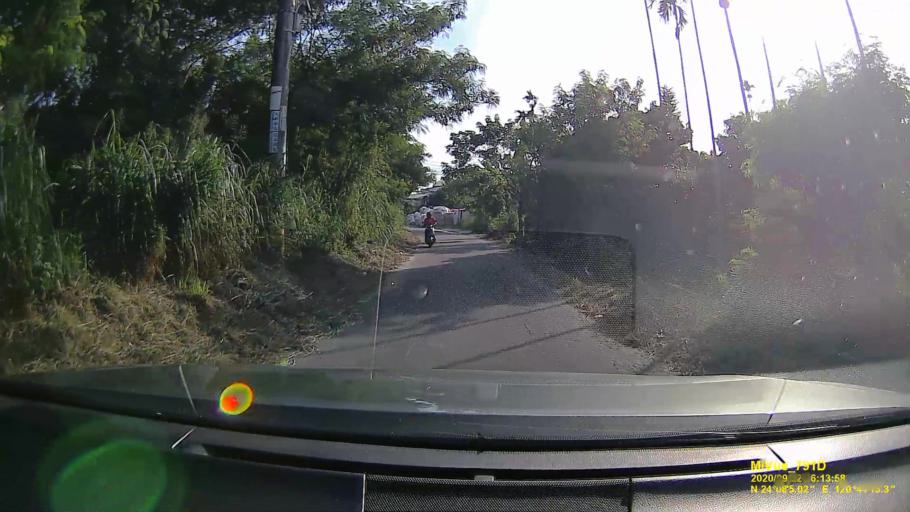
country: TW
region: Taiwan
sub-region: Taichung City
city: Taichung
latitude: 24.1347
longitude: 120.7370
